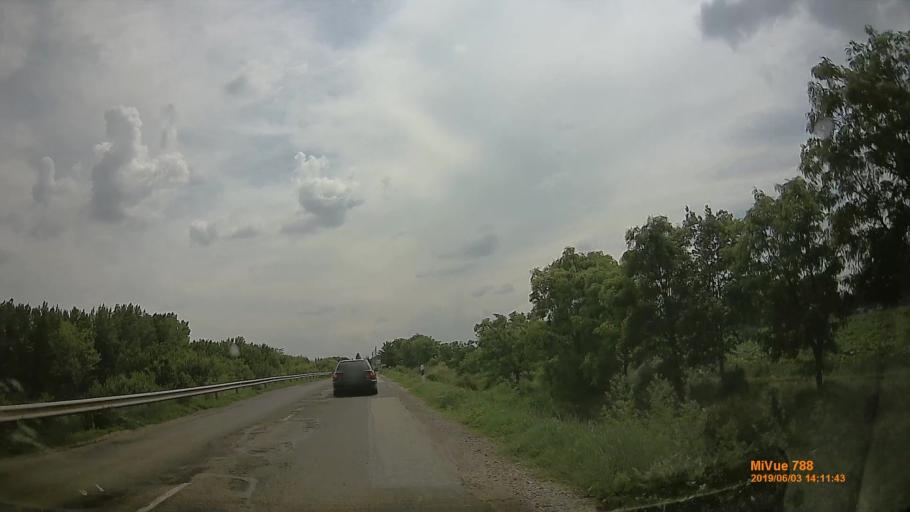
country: HU
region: Jasz-Nagykun-Szolnok
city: Toszeg
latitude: 47.1073
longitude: 20.1290
